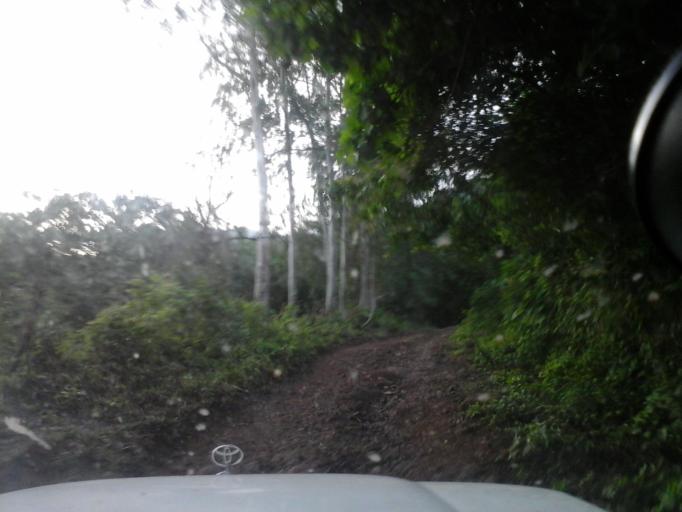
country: CO
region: Cesar
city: Agustin Codazzi
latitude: 10.1736
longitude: -73.1495
